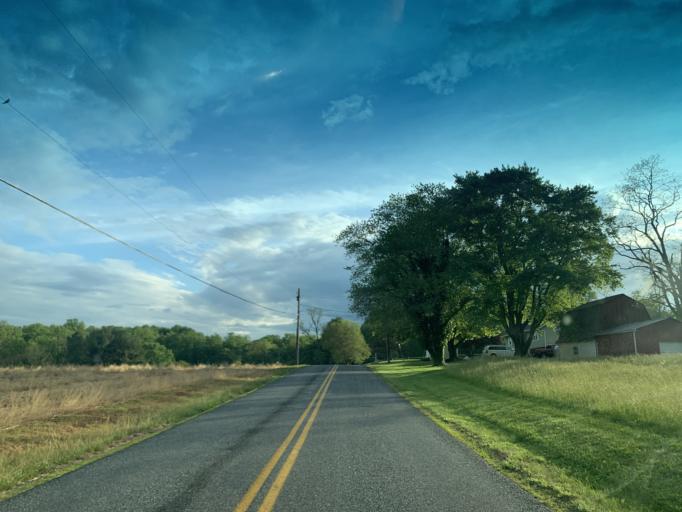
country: US
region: Pennsylvania
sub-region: York County
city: Susquehanna Trails
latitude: 39.6635
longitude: -76.2409
